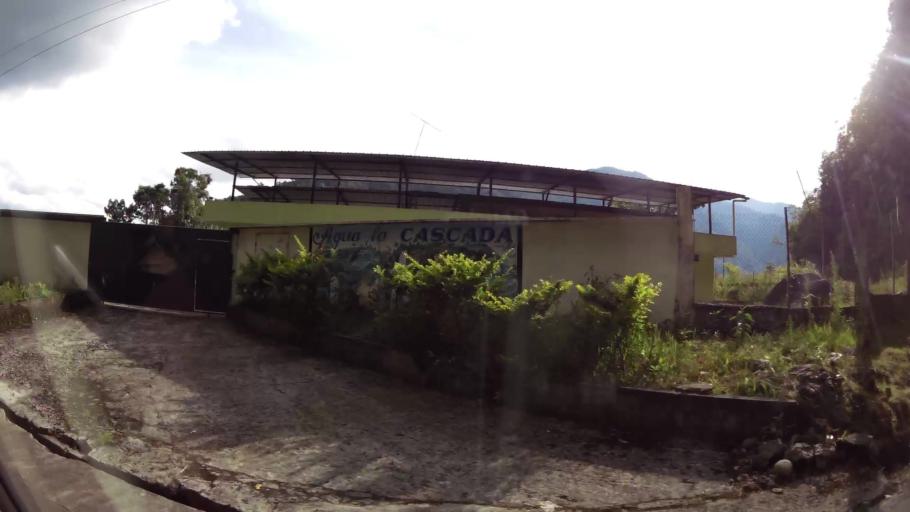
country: EC
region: Pastaza
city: Puyo
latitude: -1.4493
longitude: -78.1454
